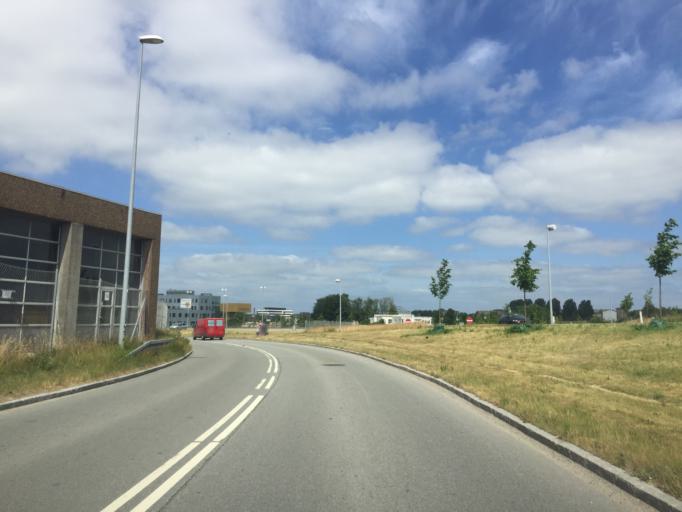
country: DK
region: Zealand
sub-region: Roskilde Kommune
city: Roskilde
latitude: 55.6236
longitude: 12.0907
